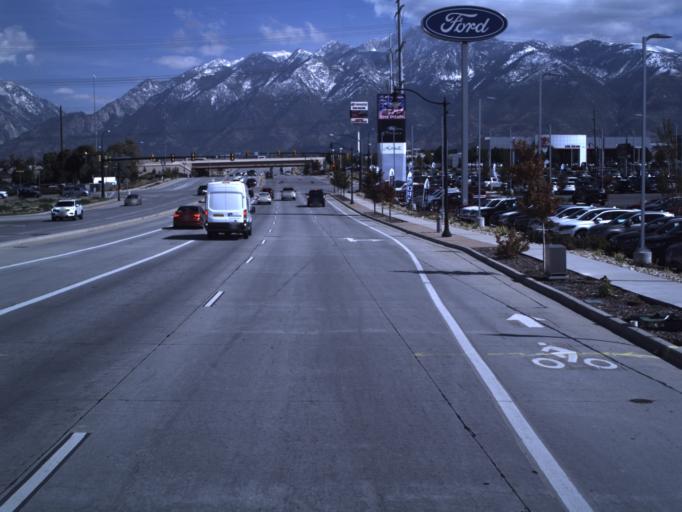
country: US
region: Utah
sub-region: Salt Lake County
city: South Jordan
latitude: 40.5442
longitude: -111.9007
